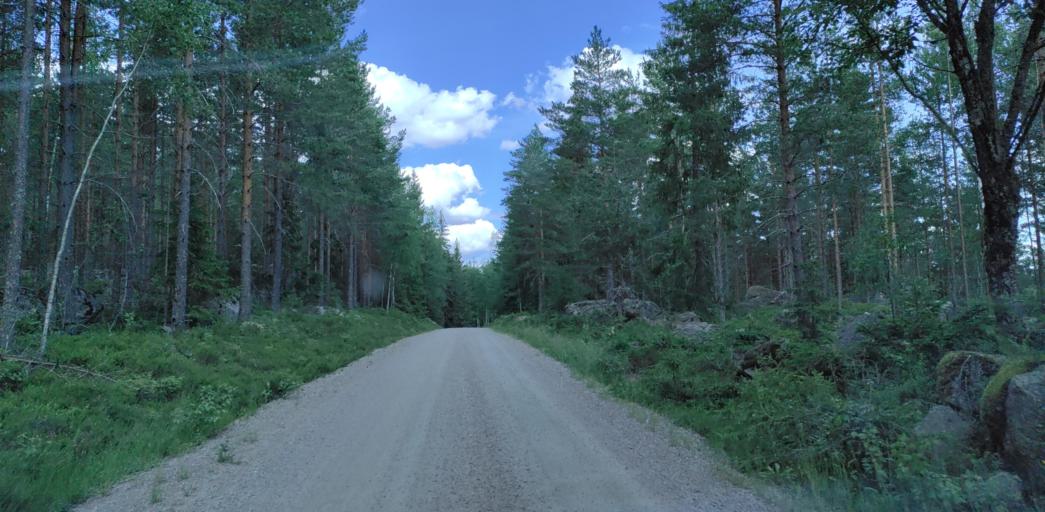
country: SE
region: Vaermland
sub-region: Hagfors Kommun
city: Ekshaerad
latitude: 60.0939
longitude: 13.4172
